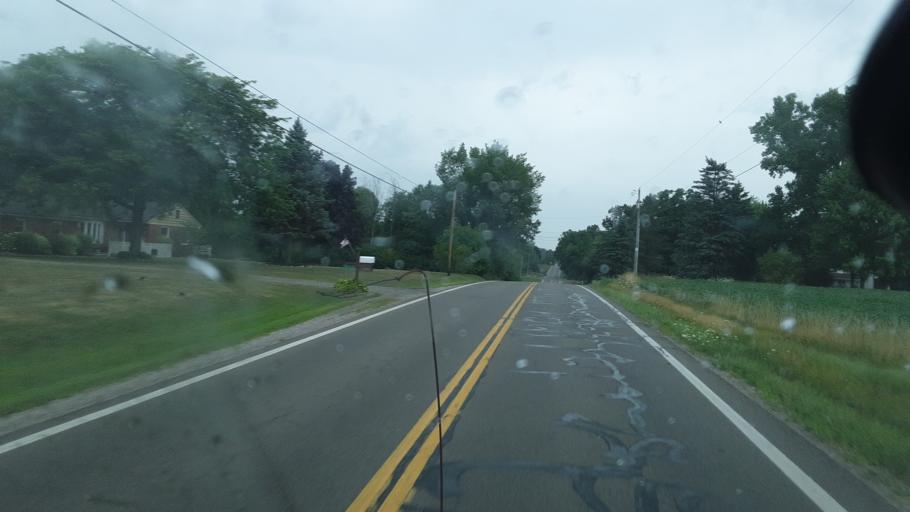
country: US
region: Ohio
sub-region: Williams County
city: Bryan
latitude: 41.4821
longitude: -84.6131
